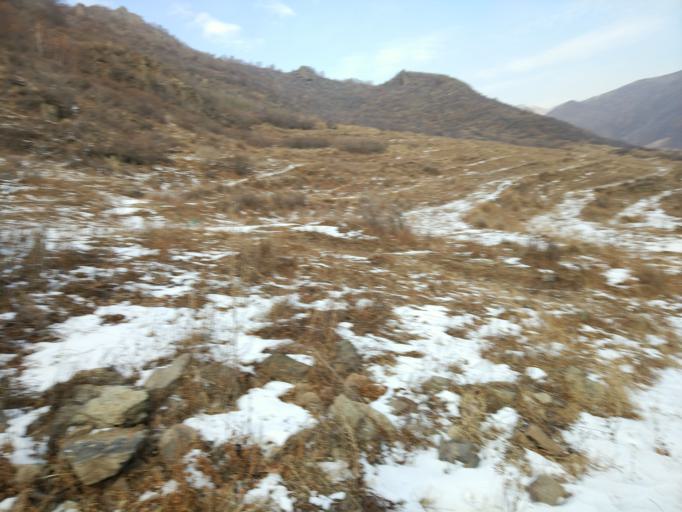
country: CN
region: Hebei
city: Xiwanzi
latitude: 40.8429
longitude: 115.4610
